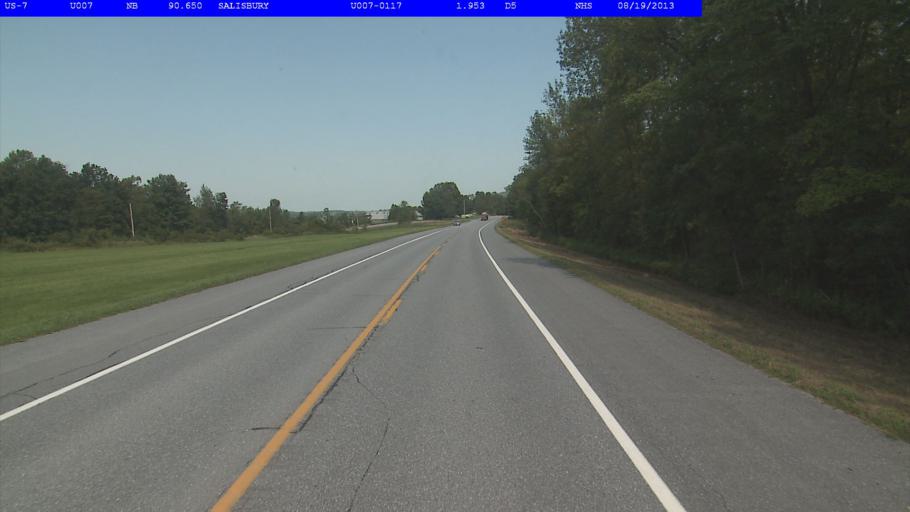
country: US
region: Vermont
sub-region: Addison County
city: Middlebury (village)
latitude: 43.9200
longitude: -73.1115
